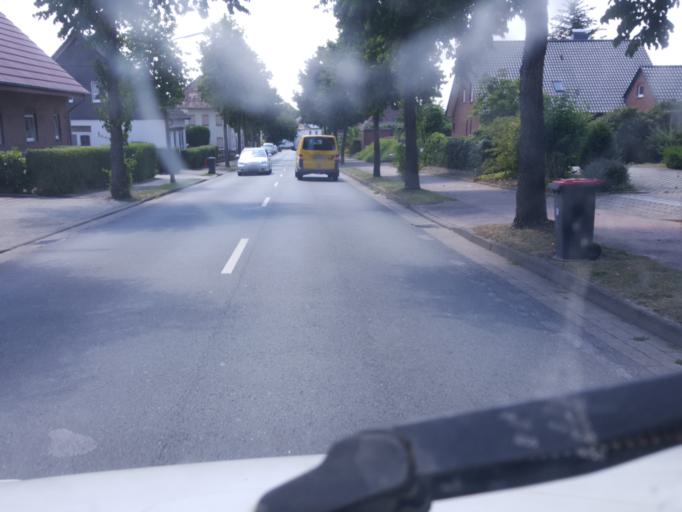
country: DE
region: North Rhine-Westphalia
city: Loehne
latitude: 52.2256
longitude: 8.7331
